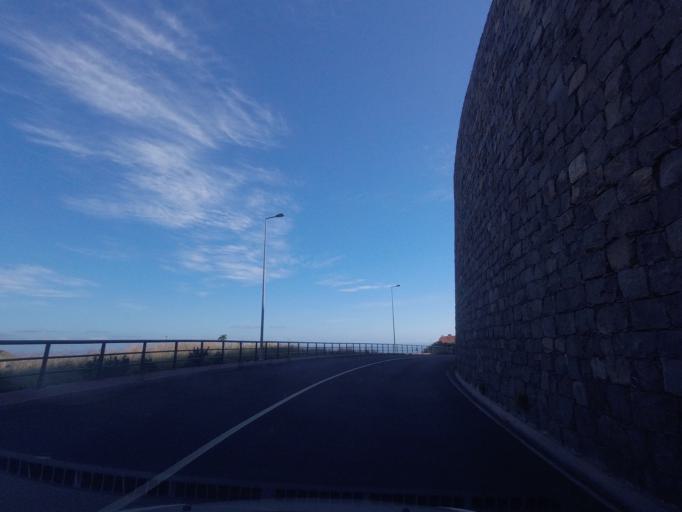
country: PT
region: Madeira
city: Canico
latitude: 32.6511
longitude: -16.8371
